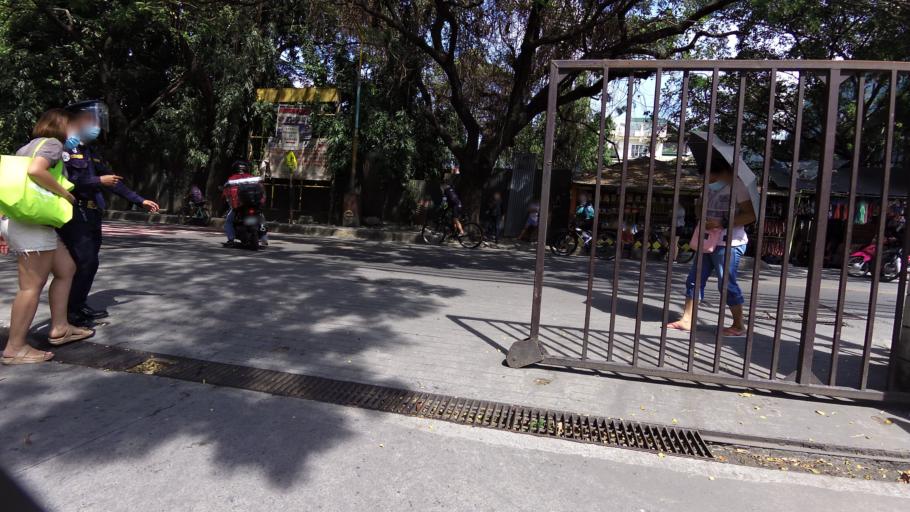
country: PH
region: Calabarzon
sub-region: Province of Rizal
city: Cainta
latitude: 14.5755
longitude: 121.0976
